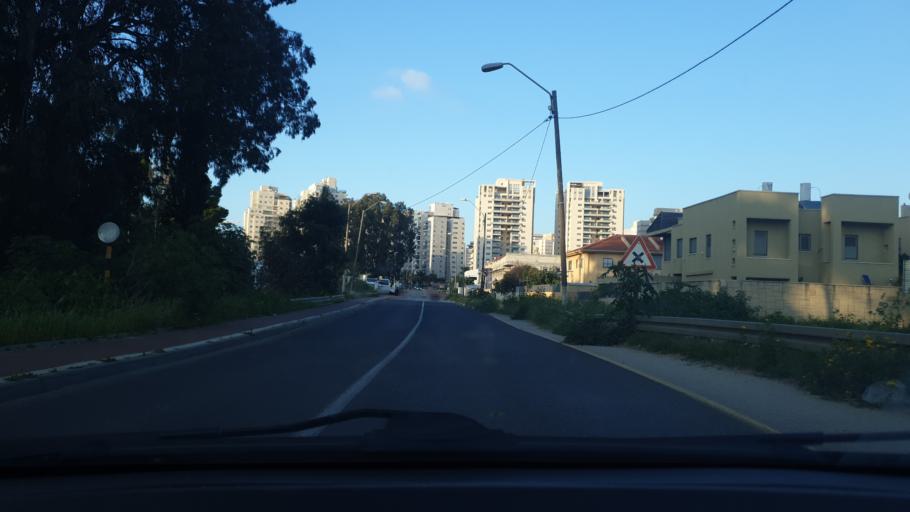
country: IL
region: Central District
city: Ness Ziona
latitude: 31.9343
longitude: 34.8312
